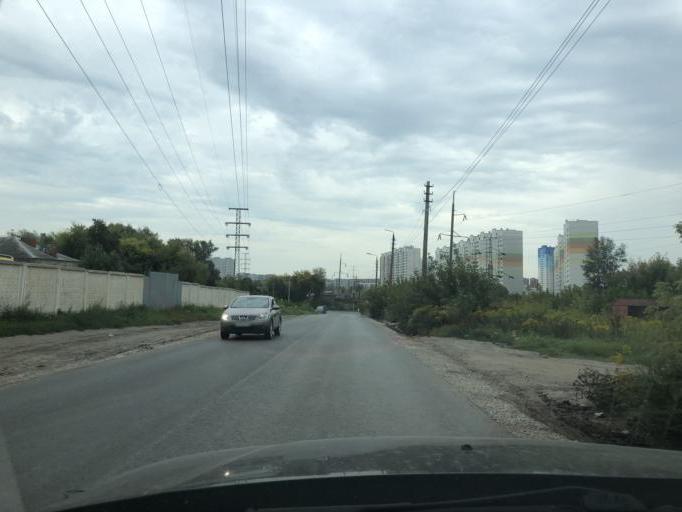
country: RU
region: Tula
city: Tula
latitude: 54.2187
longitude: 37.6746
